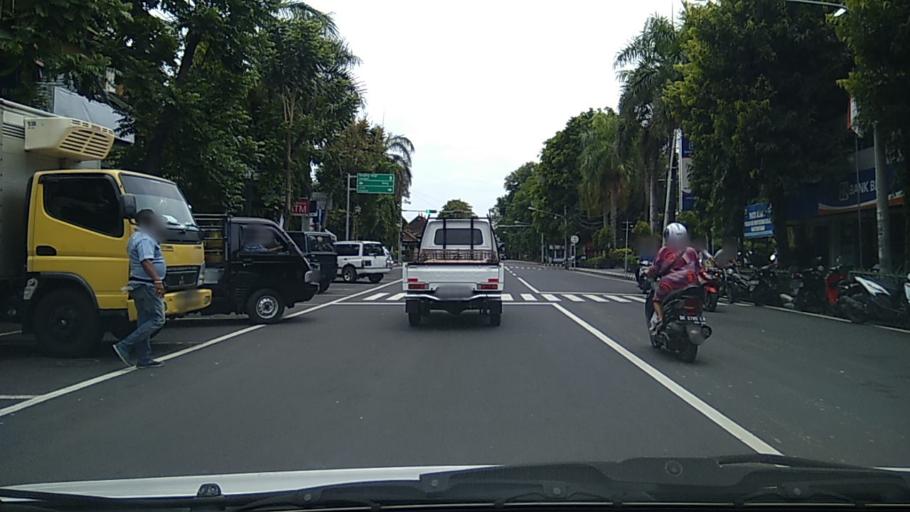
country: ID
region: Bali
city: Banjar Kelodan
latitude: -8.5416
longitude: 115.3283
